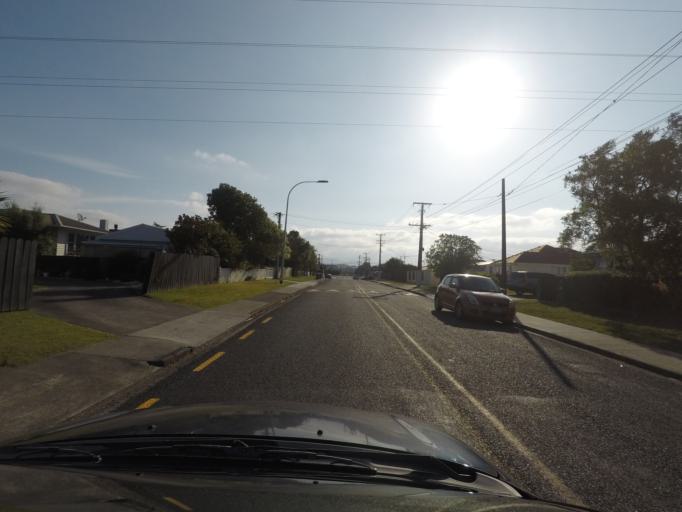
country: NZ
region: Auckland
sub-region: Auckland
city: Rosebank
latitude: -36.8565
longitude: 174.6444
